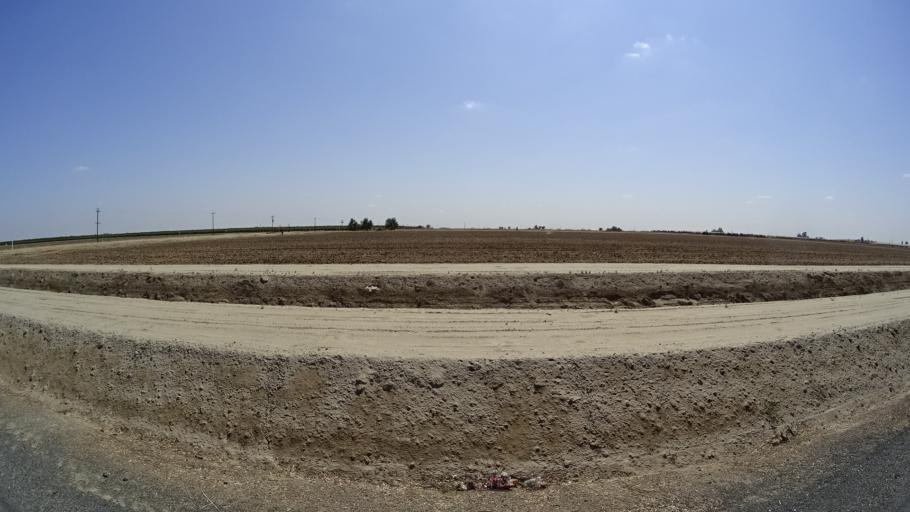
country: US
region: California
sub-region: Kings County
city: Home Garden
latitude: 36.2393
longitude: -119.6189
